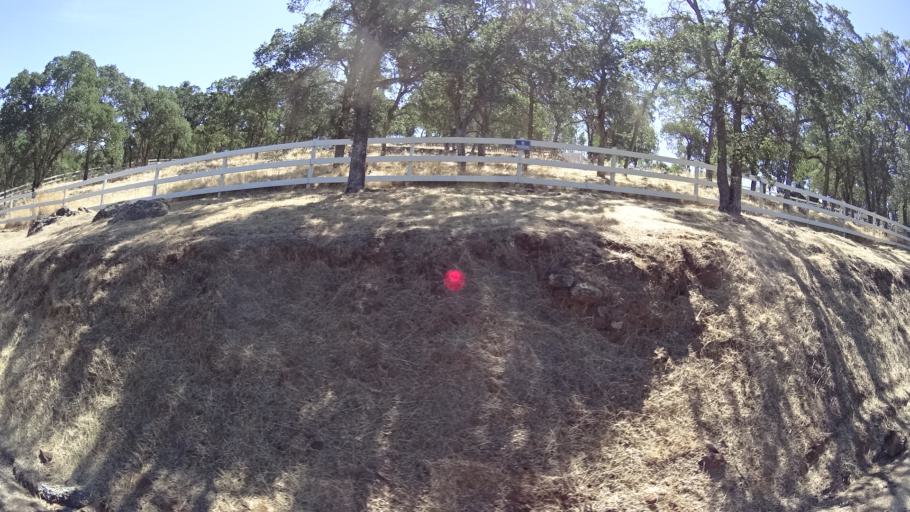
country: US
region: California
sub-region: Calaveras County
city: Rancho Calaveras
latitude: 38.1447
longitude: -120.8530
